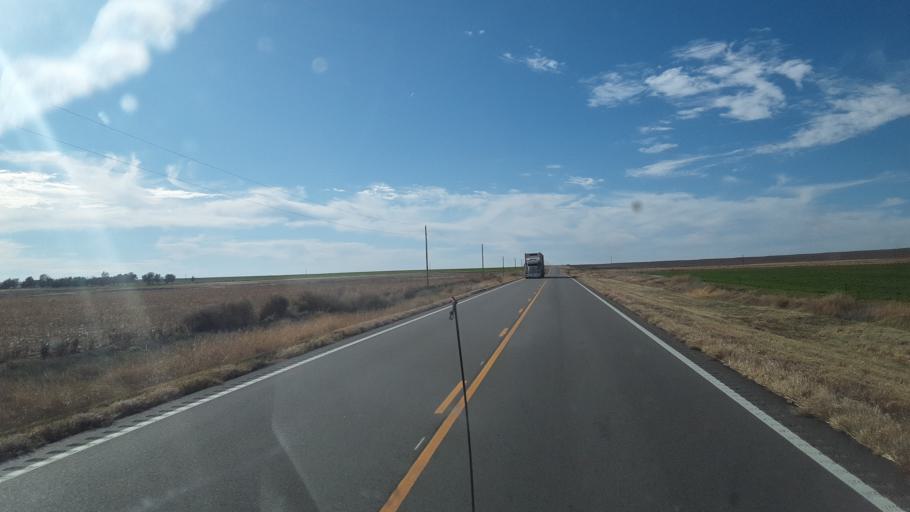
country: US
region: Kansas
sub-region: Hodgeman County
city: Jetmore
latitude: 38.0727
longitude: -100.0208
